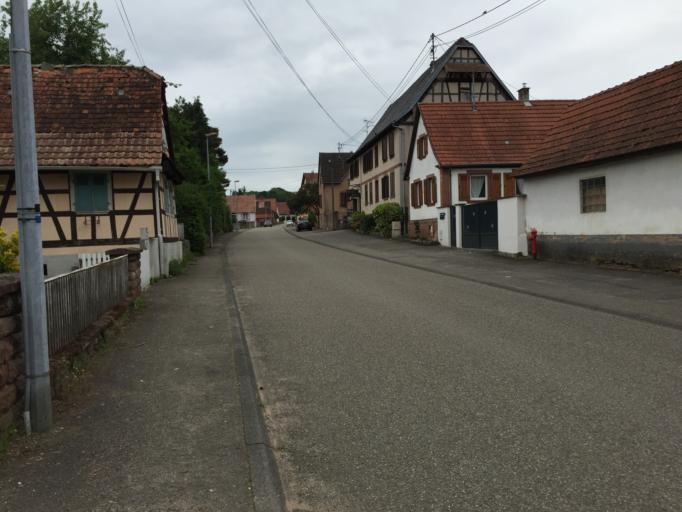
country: FR
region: Alsace
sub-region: Departement du Bas-Rhin
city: Gundershoffen
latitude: 48.9049
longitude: 7.6618
